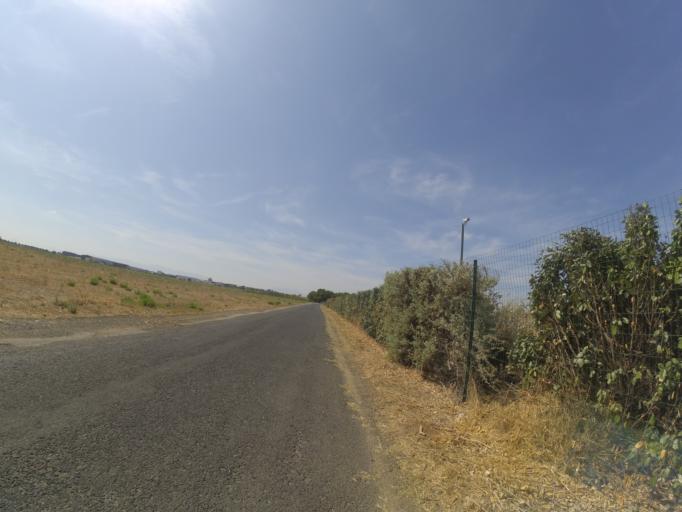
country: FR
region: Languedoc-Roussillon
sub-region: Departement des Pyrenees-Orientales
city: Rivesaltes
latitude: 42.7942
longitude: 2.8976
